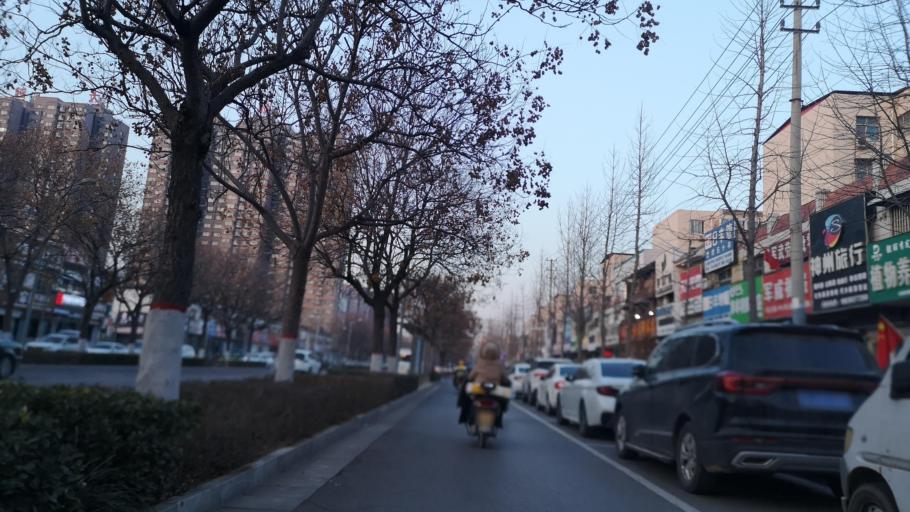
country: CN
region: Henan Sheng
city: Puyang
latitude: 35.7702
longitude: 115.0143
